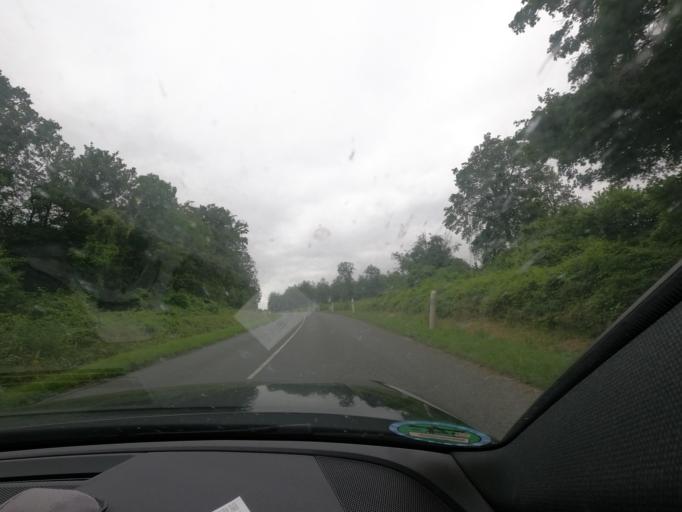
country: FR
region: Picardie
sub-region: Departement de l'Oise
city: Ressons-sur-Matz
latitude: 49.5270
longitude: 2.7175
